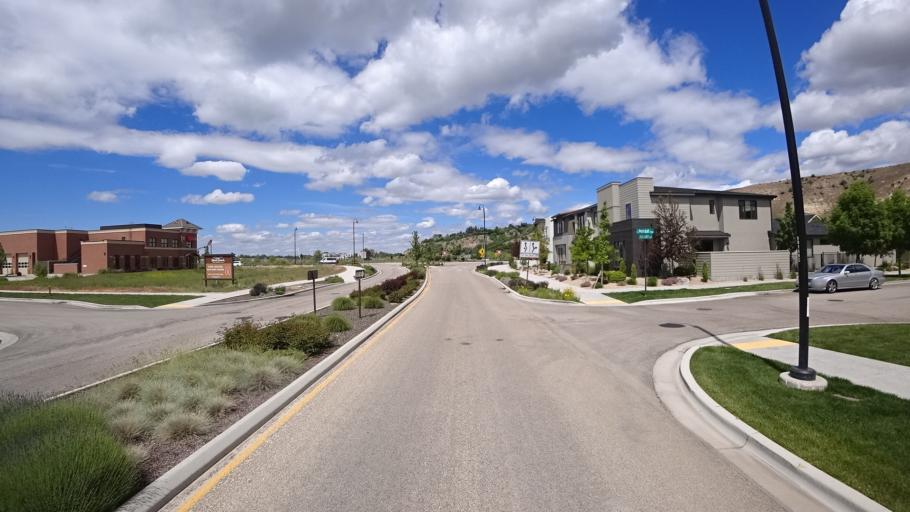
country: US
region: Idaho
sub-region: Ada County
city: Boise
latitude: 43.5761
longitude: -116.1387
